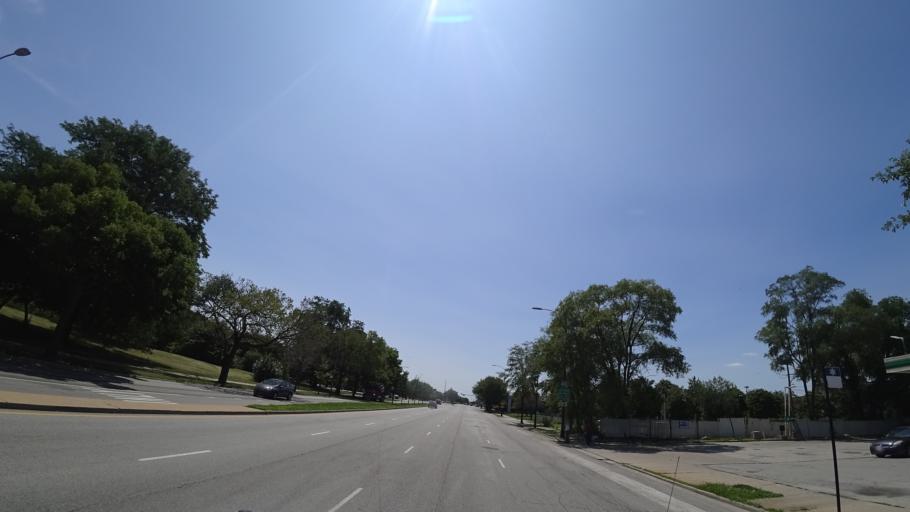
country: US
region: Illinois
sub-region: Cook County
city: Chicago
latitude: 41.7749
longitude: -87.5863
